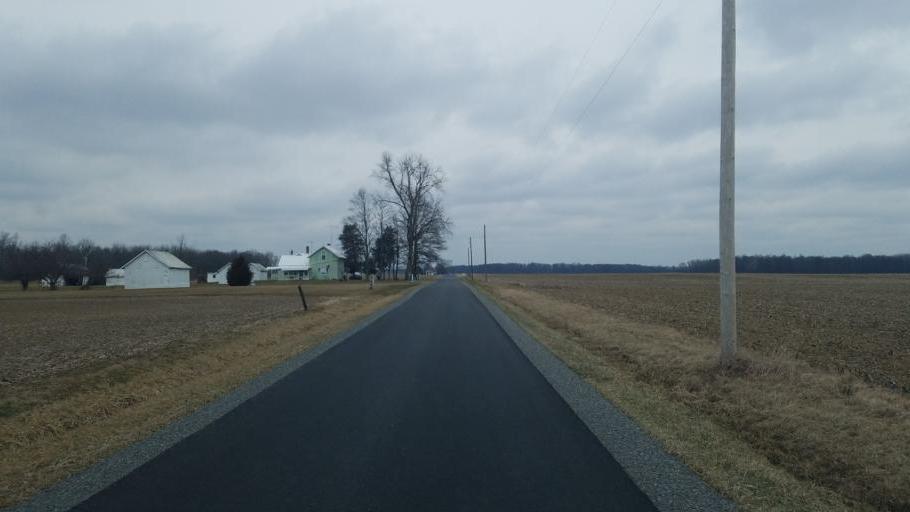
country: US
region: Ohio
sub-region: Morrow County
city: Mount Gilead
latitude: 40.5896
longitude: -82.8950
